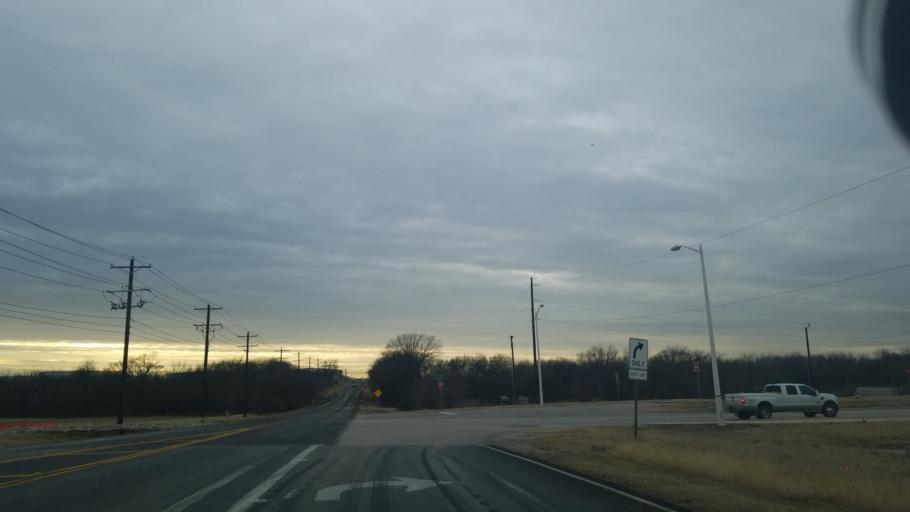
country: US
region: Texas
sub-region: Denton County
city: Denton
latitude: 33.2019
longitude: -97.1849
